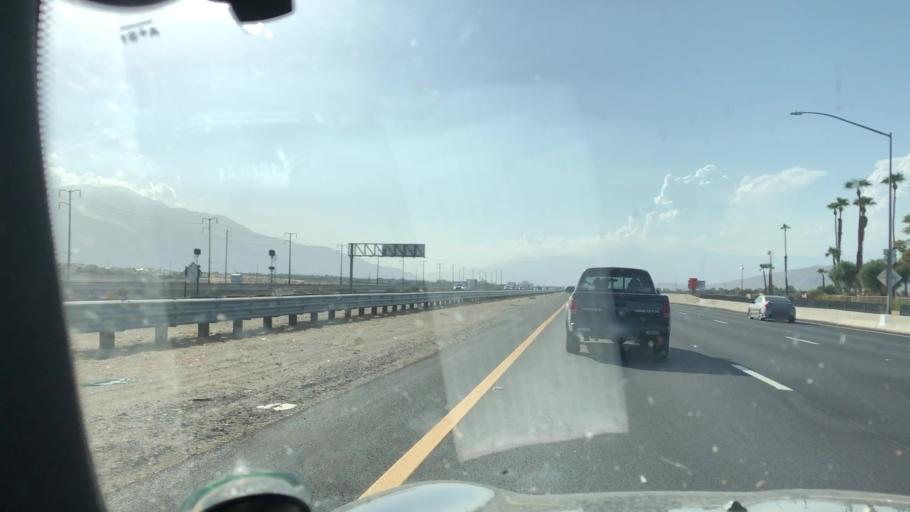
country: US
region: California
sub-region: Riverside County
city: Thousand Palms
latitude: 33.7898
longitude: -116.3608
